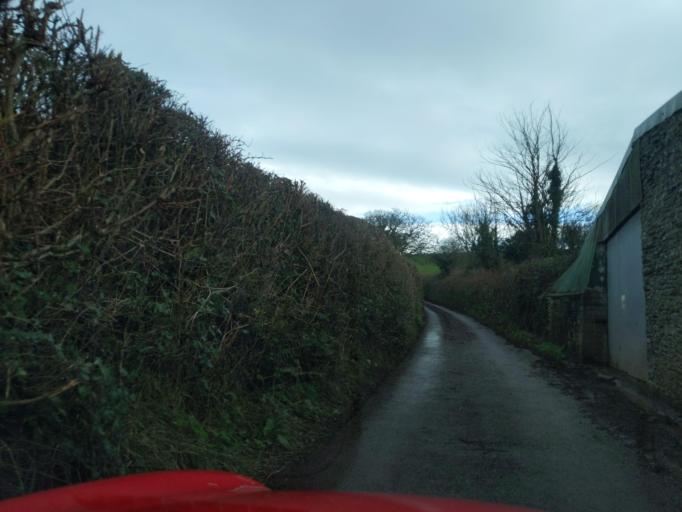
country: GB
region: England
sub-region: Devon
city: Salcombe
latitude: 50.2672
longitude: -3.6932
